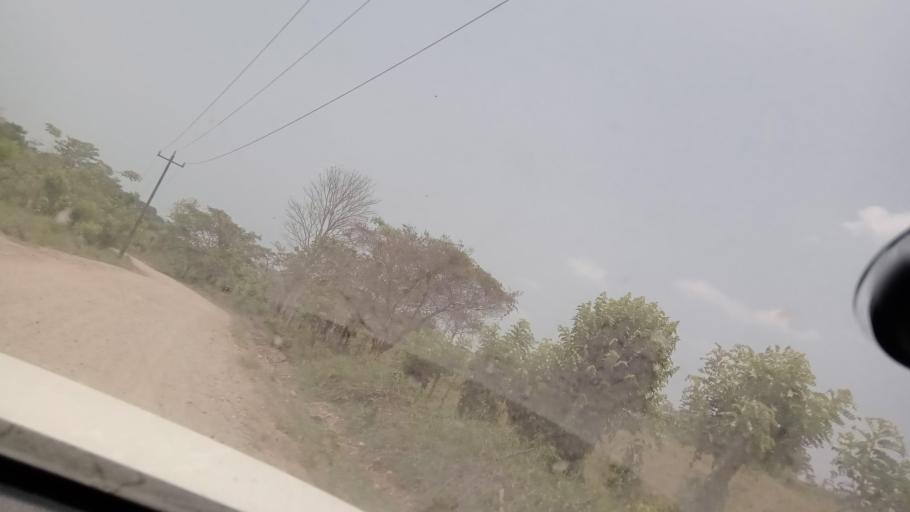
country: MX
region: Chiapas
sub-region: Tecpatan
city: Raudales Malpaso
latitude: 17.4224
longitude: -93.7920
